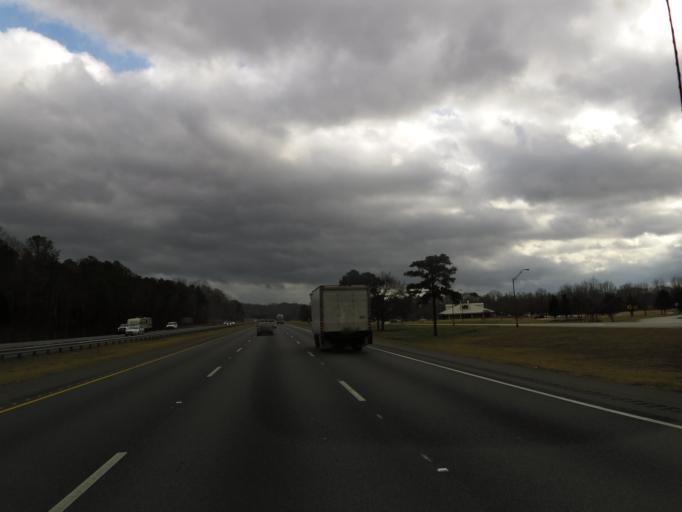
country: US
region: Georgia
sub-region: Catoosa County
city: Indian Springs
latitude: 34.9520
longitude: -85.1773
